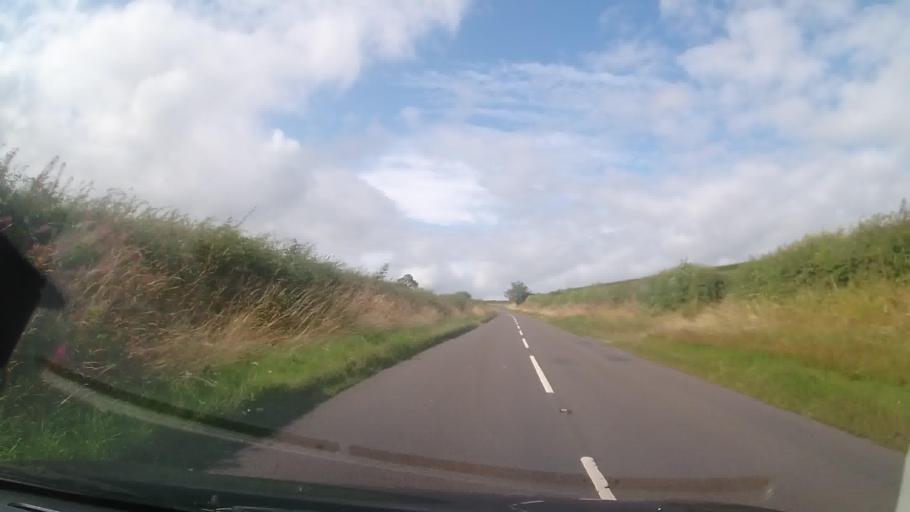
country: GB
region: Wales
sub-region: Sir Powys
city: Knighton
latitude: 52.3859
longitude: -3.0399
